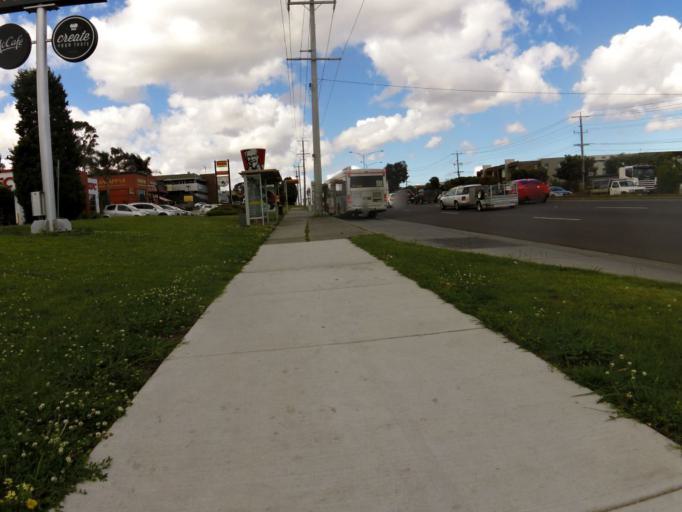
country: AU
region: Victoria
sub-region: Knox
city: Rowville
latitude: -37.9179
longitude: 145.2353
